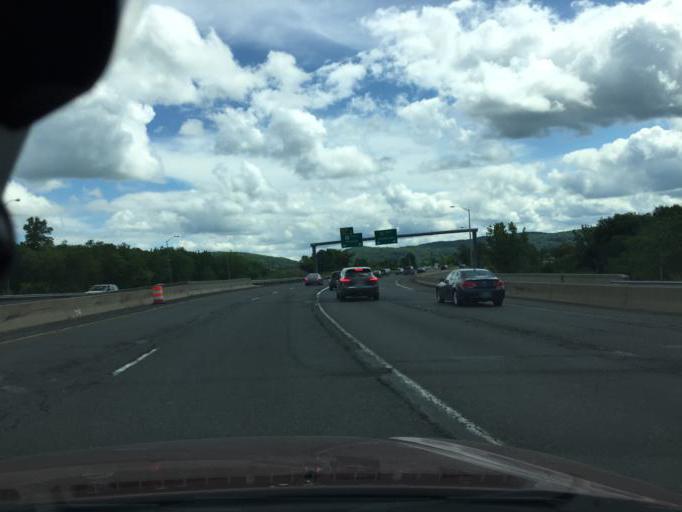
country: US
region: Connecticut
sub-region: Fairfield County
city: Danbury
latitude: 41.3889
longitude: -73.4762
